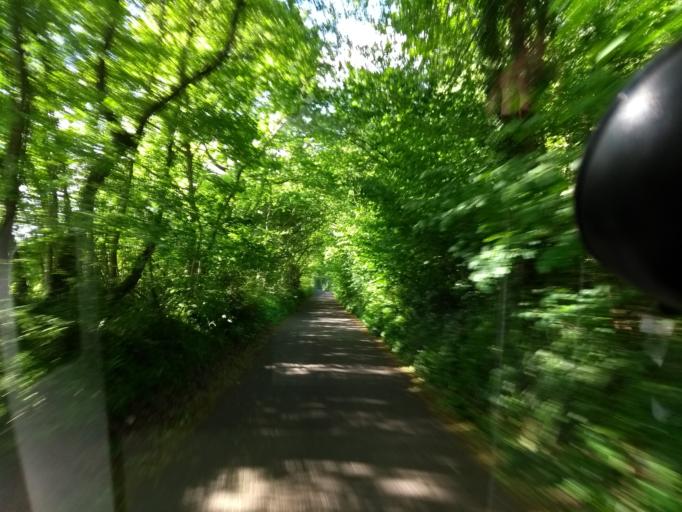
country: GB
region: England
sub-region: Somerset
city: Taunton
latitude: 50.9743
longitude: -3.1060
